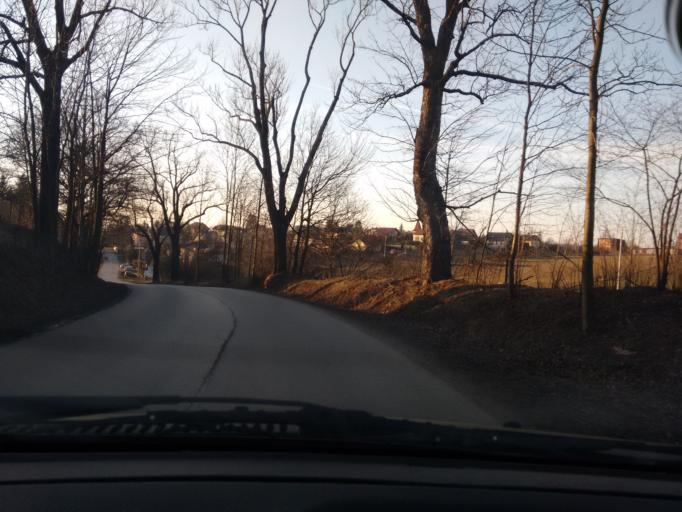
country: PL
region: Silesian Voivodeship
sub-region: Powiat cieszynski
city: Puncow
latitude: 49.7480
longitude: 18.6706
